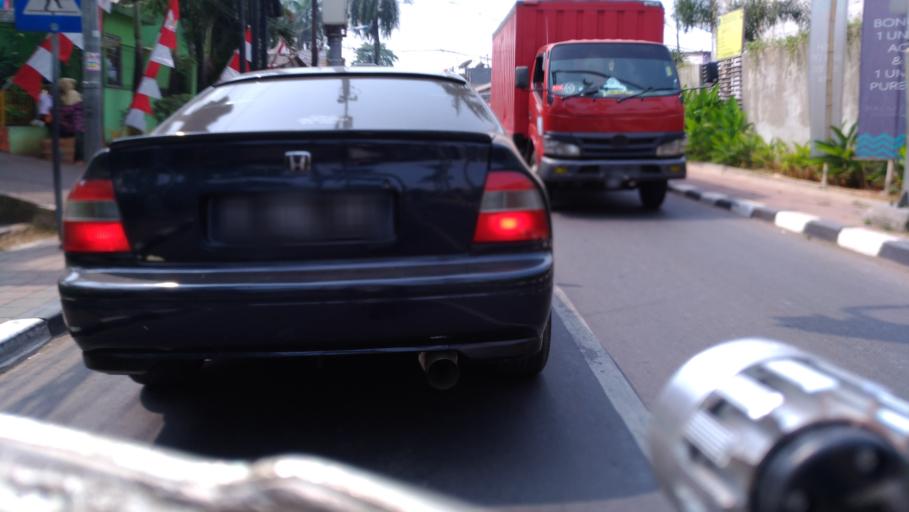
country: ID
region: West Java
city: Cileungsir
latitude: -6.3150
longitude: 106.9000
